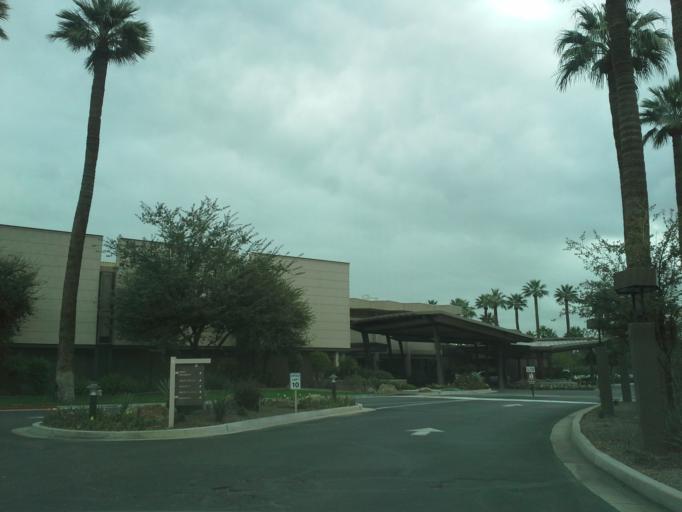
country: US
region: Arizona
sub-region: Maricopa County
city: Phoenix
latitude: 33.4819
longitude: -112.0644
